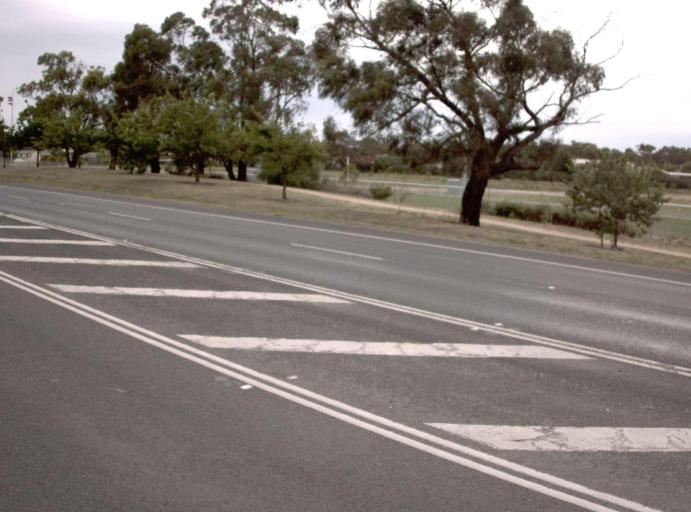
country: AU
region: Victoria
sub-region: Casey
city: Cranbourne
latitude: -38.1198
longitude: 145.2877
